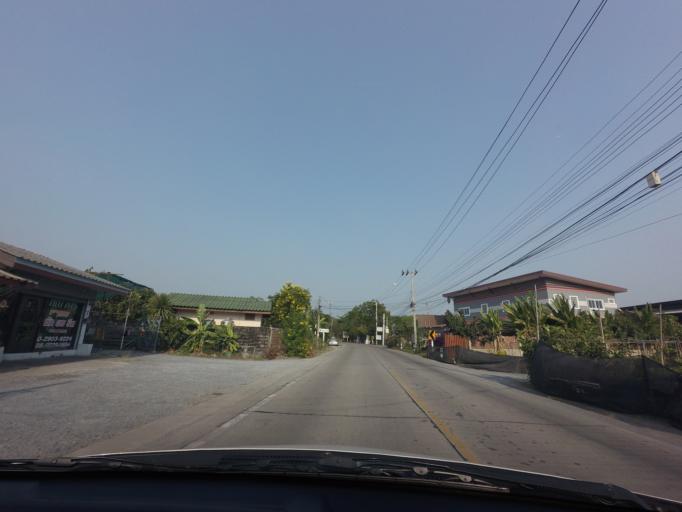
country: TH
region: Nonthaburi
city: Bang Yai
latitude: 13.8052
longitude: 100.3937
